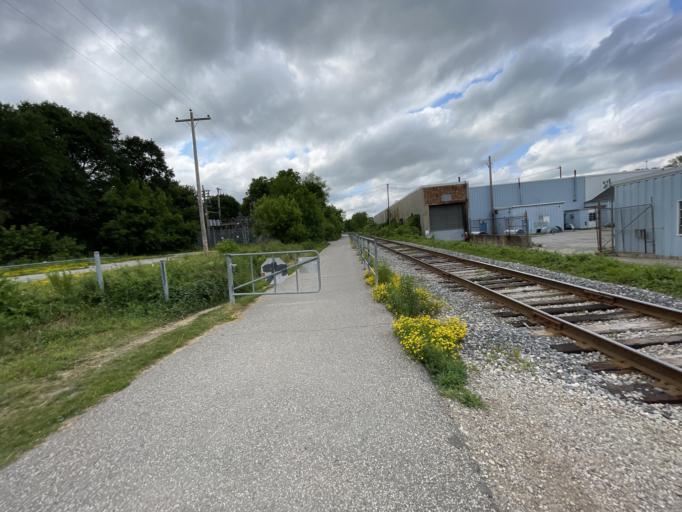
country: CA
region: Ontario
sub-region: Wellington County
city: Guelph
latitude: 43.5555
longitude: -80.2605
